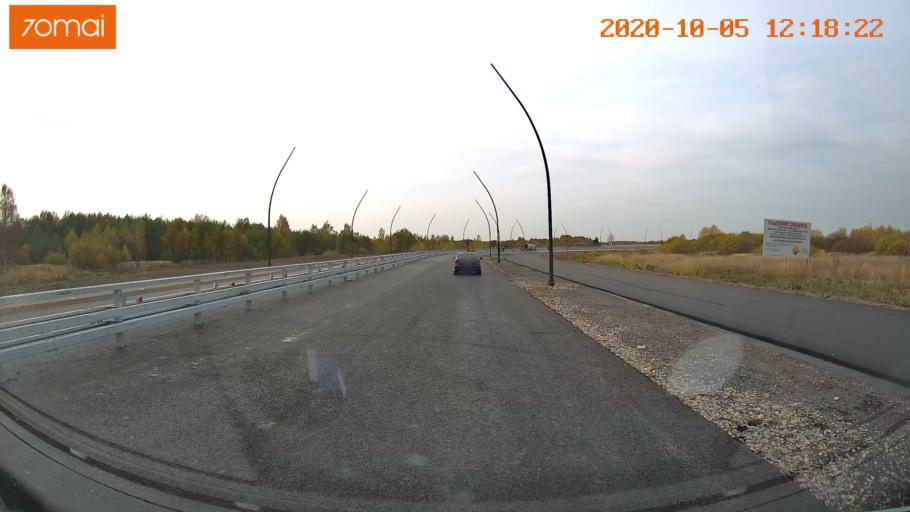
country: RU
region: Ivanovo
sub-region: Gorod Ivanovo
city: Ivanovo
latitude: 56.9520
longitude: 40.9424
